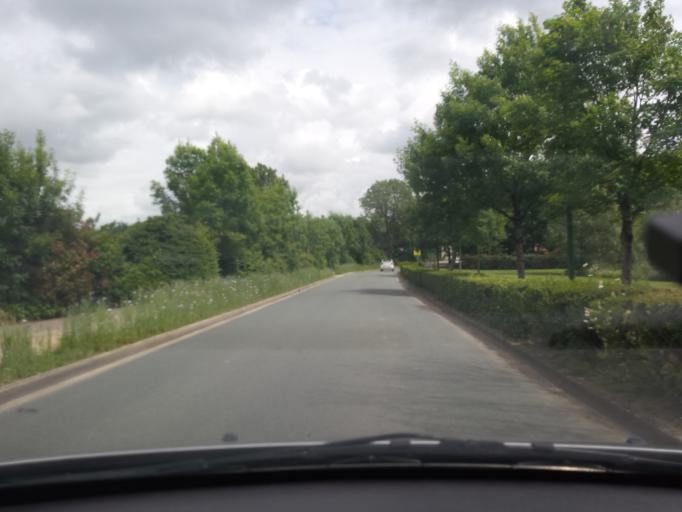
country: FR
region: Pays de la Loire
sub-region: Departement de la Vendee
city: Landeronde
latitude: 46.6597
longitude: -1.5768
